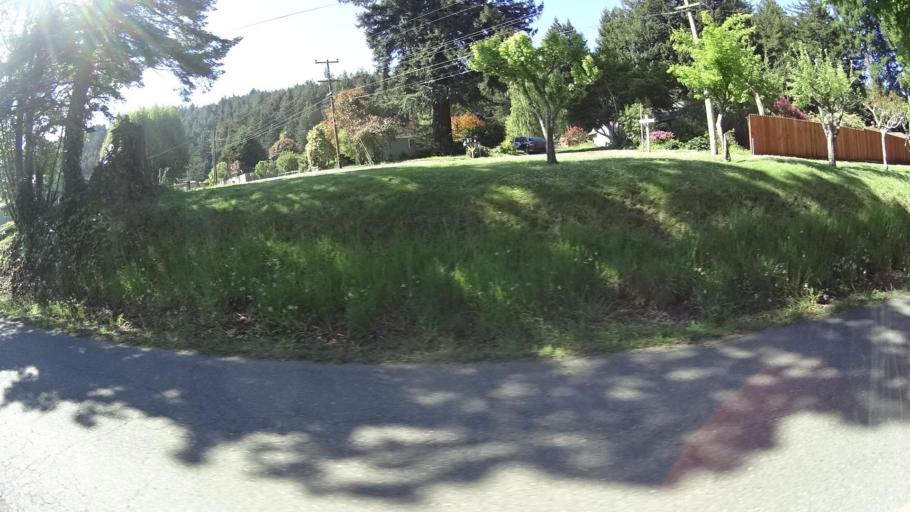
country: US
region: California
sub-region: Humboldt County
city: Rio Dell
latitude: 40.5071
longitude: -124.1241
